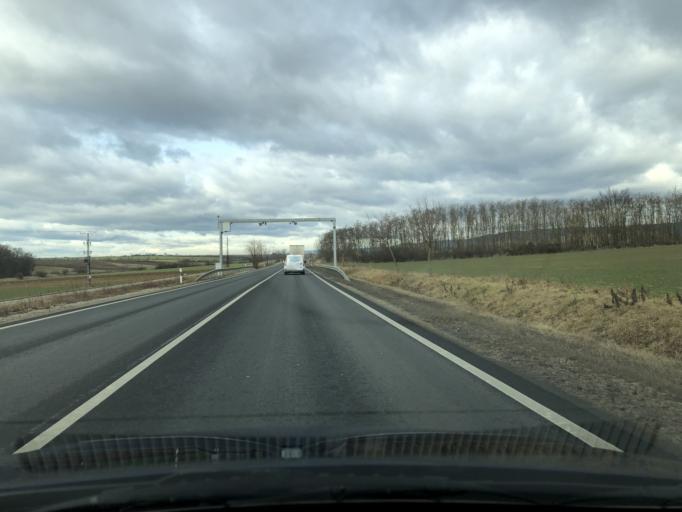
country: AT
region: Burgenland
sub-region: Politischer Bezirk Oberwart
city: Schachendorf
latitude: 47.2473
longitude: 16.4820
